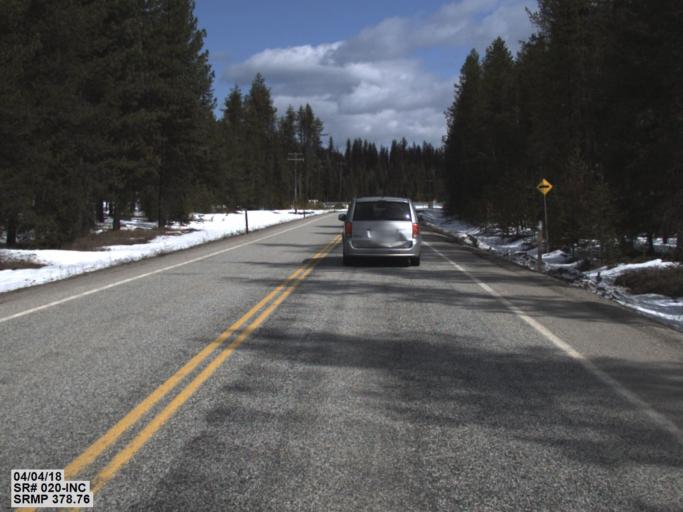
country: US
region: Washington
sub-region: Stevens County
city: Colville
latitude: 48.6063
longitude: -117.5499
